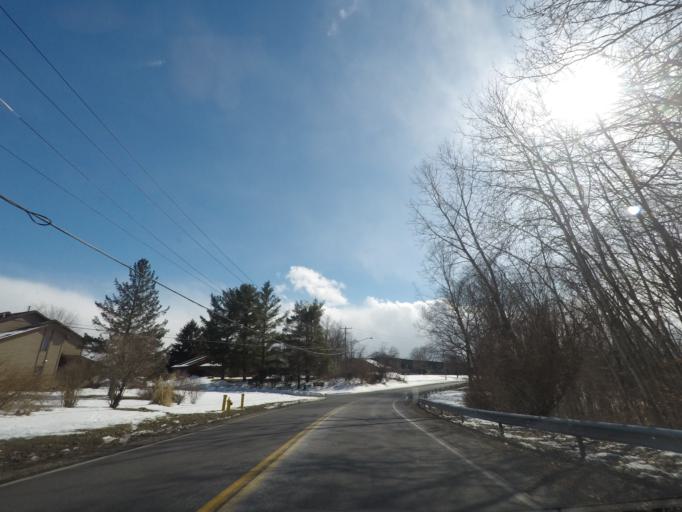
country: US
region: New York
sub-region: Albany County
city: McKownville
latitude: 42.6551
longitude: -73.8488
